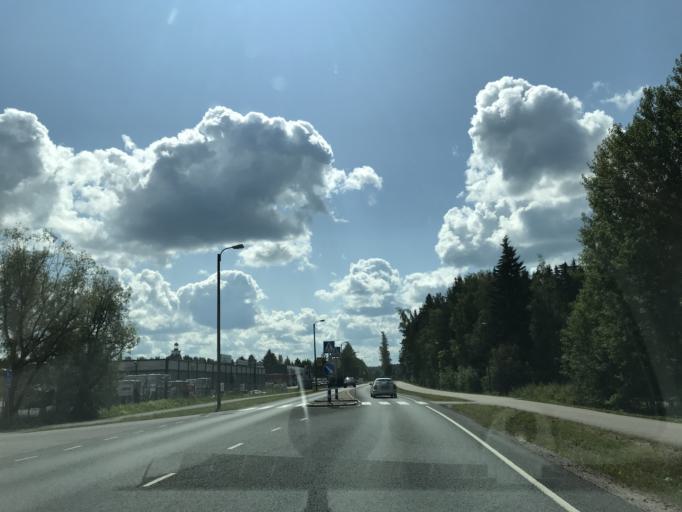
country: FI
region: Paijanne Tavastia
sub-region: Lahti
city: Orimattila
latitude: 60.8146
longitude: 25.7301
